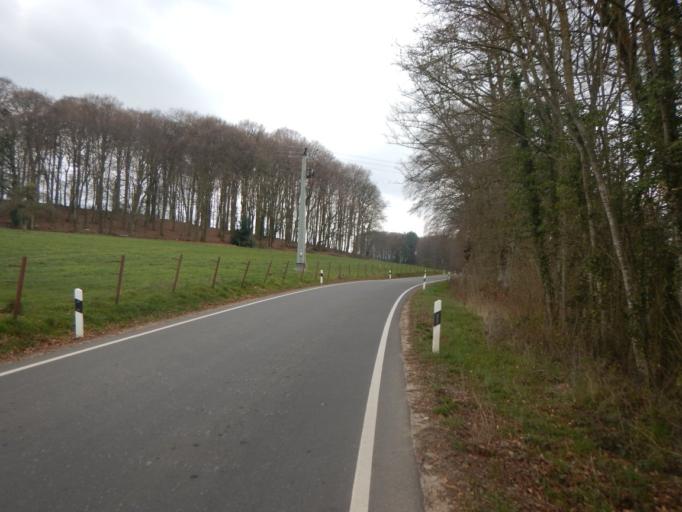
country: LU
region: Diekirch
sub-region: Canton de Redange
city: Ell
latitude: 49.7862
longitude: 5.8538
